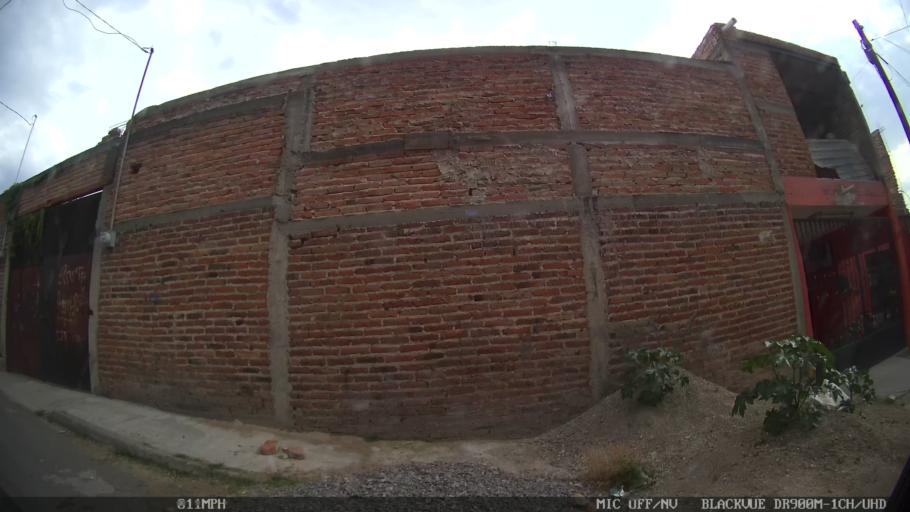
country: MX
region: Jalisco
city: Tlaquepaque
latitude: 20.6234
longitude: -103.2675
